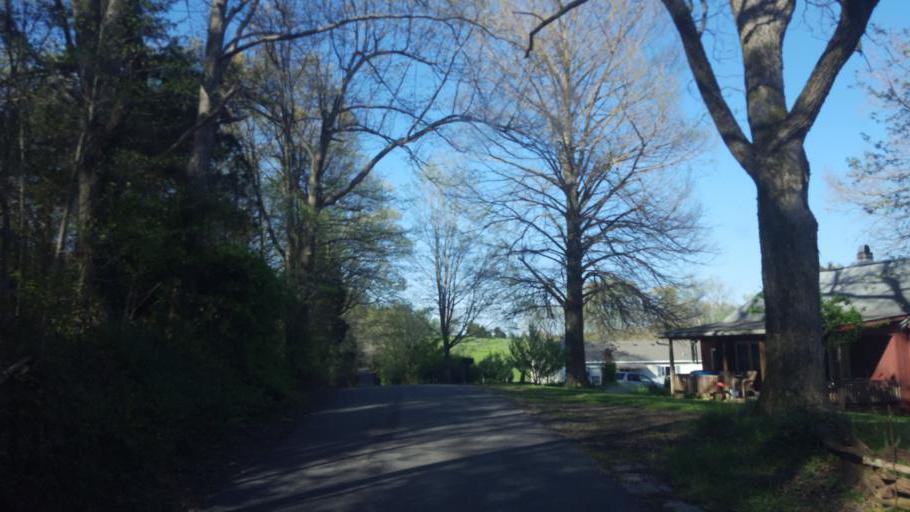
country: US
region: Kentucky
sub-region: Barren County
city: Cave City
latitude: 37.1906
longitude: -86.0484
